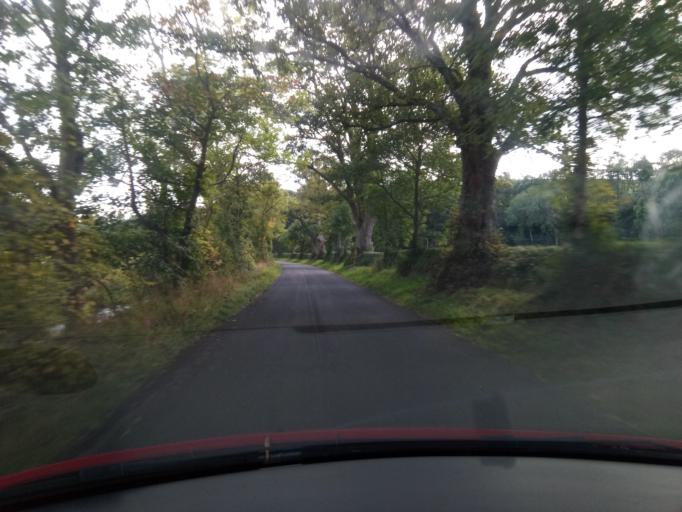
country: GB
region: Scotland
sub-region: The Scottish Borders
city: Kelso
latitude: 55.5079
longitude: -2.3515
